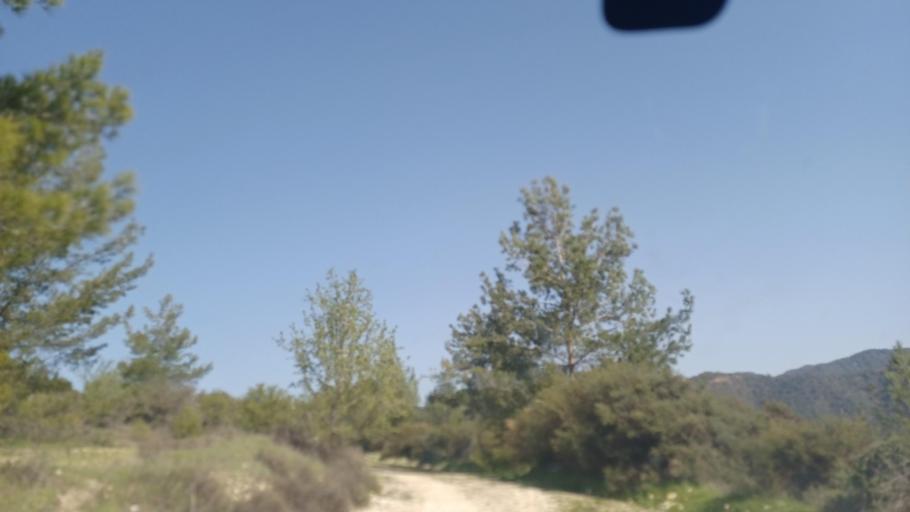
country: CY
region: Limassol
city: Pachna
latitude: 34.8838
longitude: 32.7324
